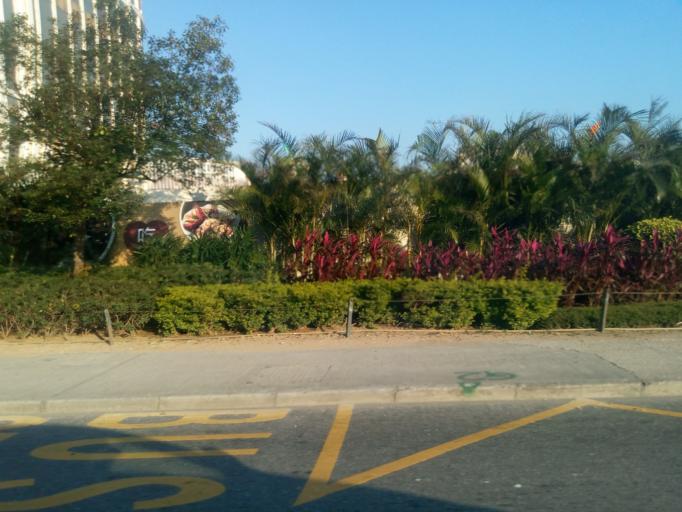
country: MO
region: Macau
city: Macau
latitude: 22.1454
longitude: 113.5528
